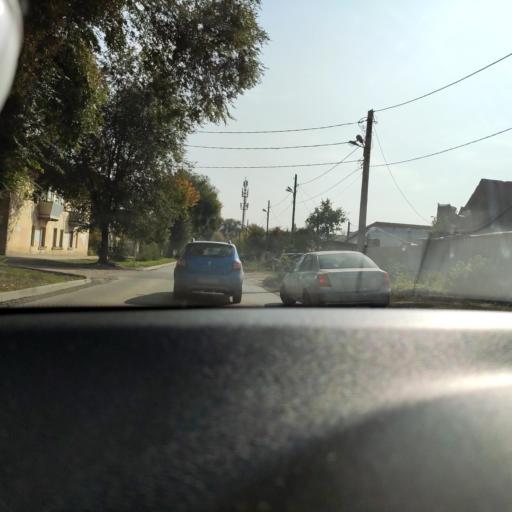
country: RU
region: Samara
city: Samara
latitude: 53.2261
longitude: 50.2505
